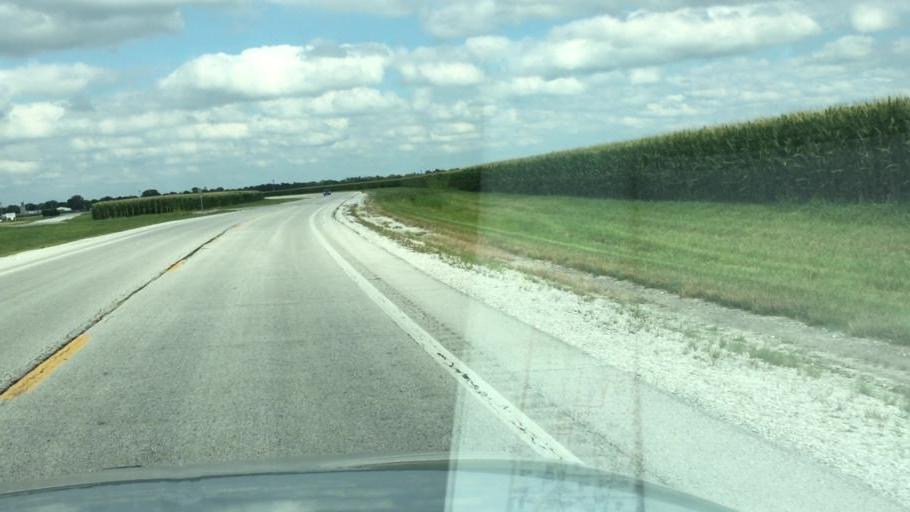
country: US
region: Illinois
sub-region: Hancock County
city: Carthage
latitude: 40.4088
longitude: -91.1656
